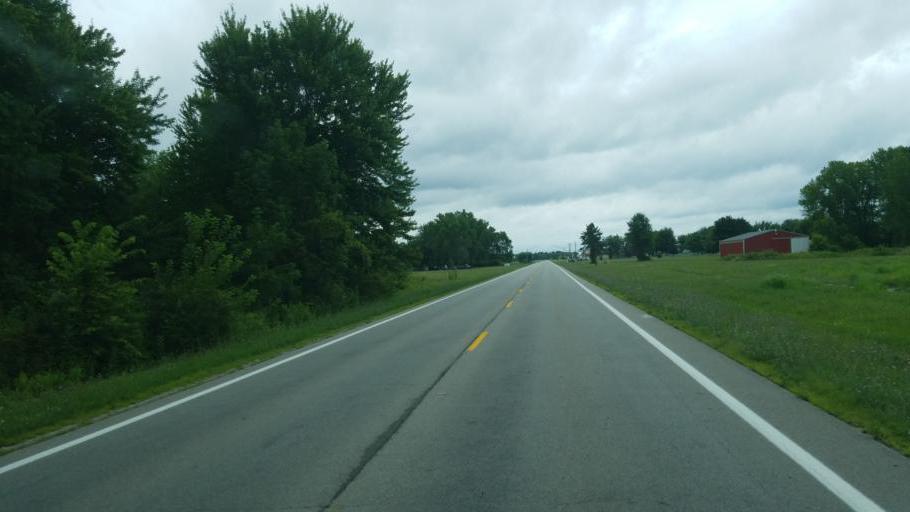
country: US
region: Ohio
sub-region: Franklin County
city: Groveport
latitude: 39.8373
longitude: -82.9132
